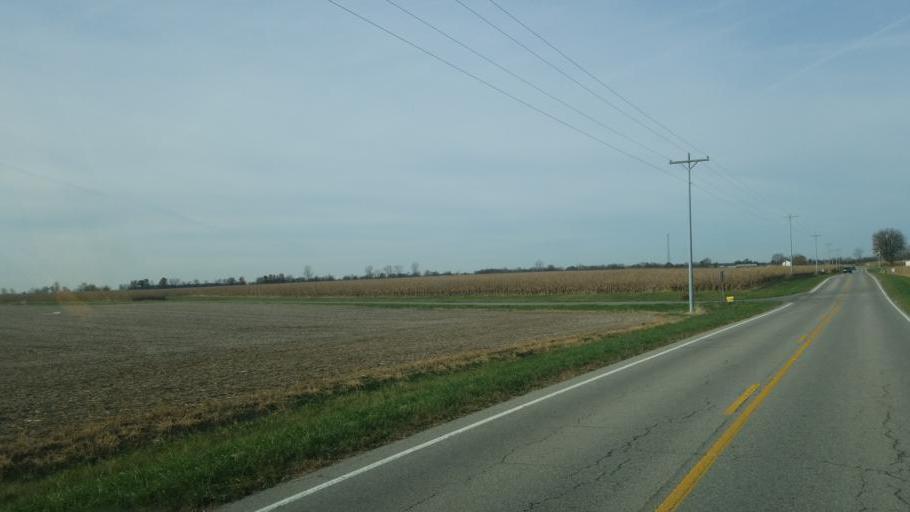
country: US
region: Ohio
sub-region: Union County
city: Marysville
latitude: 40.1465
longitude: -83.3612
